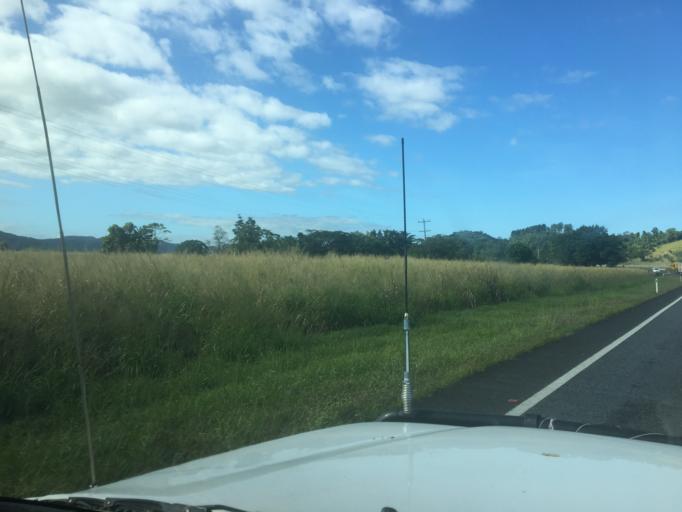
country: AU
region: Queensland
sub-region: Cassowary Coast
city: Innisfail
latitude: -17.2814
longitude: 145.9213
